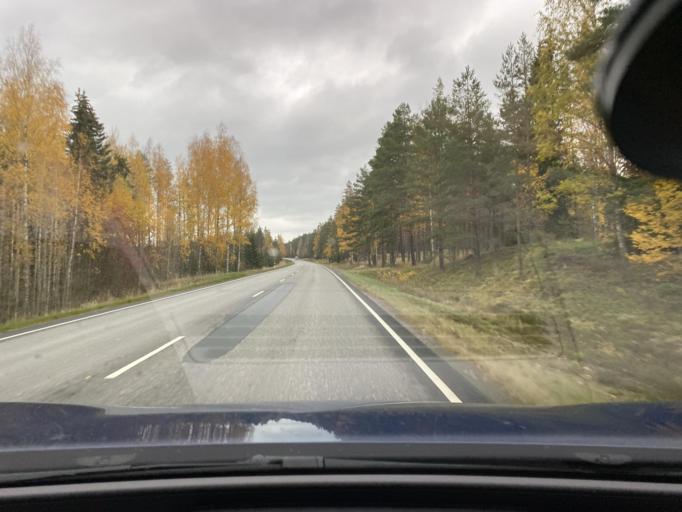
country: FI
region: Varsinais-Suomi
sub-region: Loimaa
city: Ylaene
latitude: 60.9170
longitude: 22.4171
